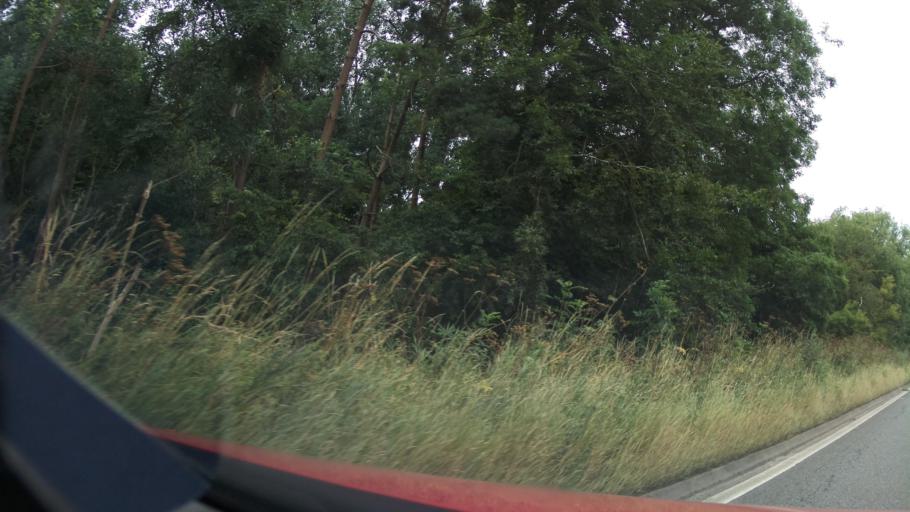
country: GB
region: England
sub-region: Northamptonshire
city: Kettering
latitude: 52.4303
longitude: -0.7332
